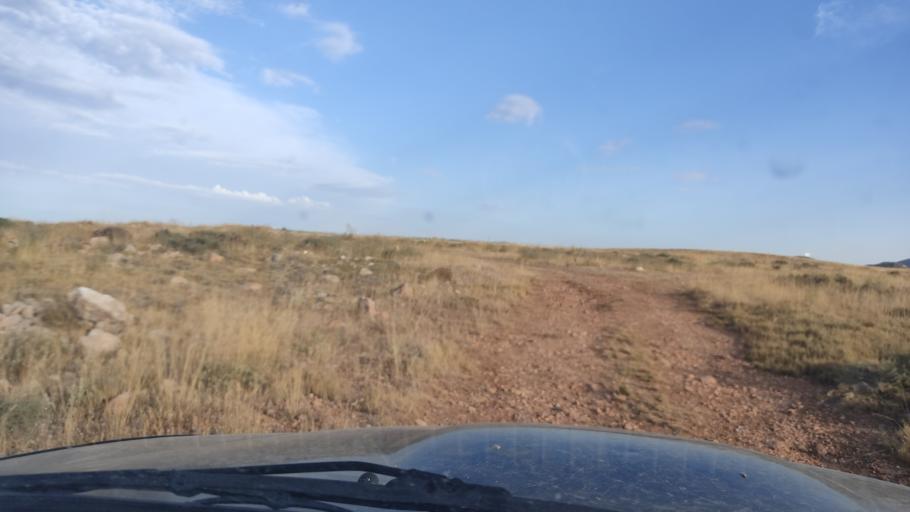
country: ES
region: Aragon
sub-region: Provincia de Teruel
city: Monforte de Moyuela
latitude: 41.0614
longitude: -0.9716
